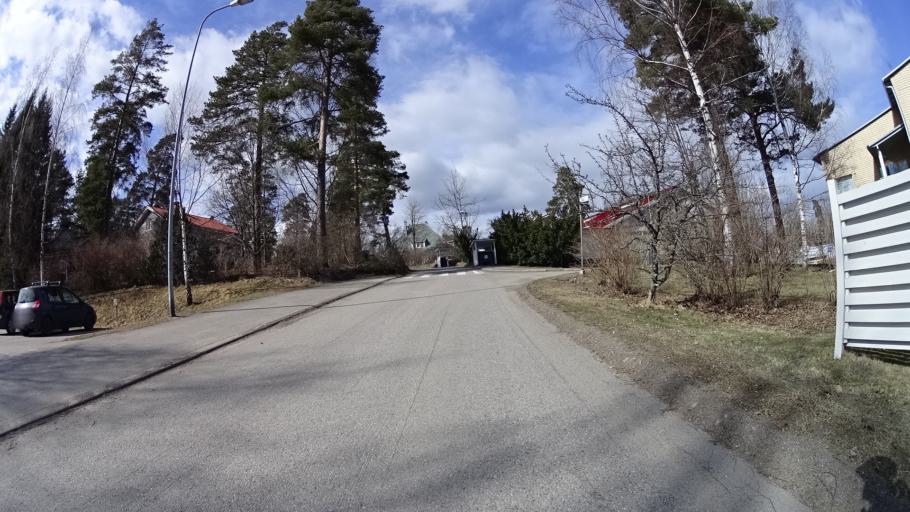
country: FI
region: Uusimaa
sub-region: Helsinki
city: Kauniainen
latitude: 60.2046
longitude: 24.7291
